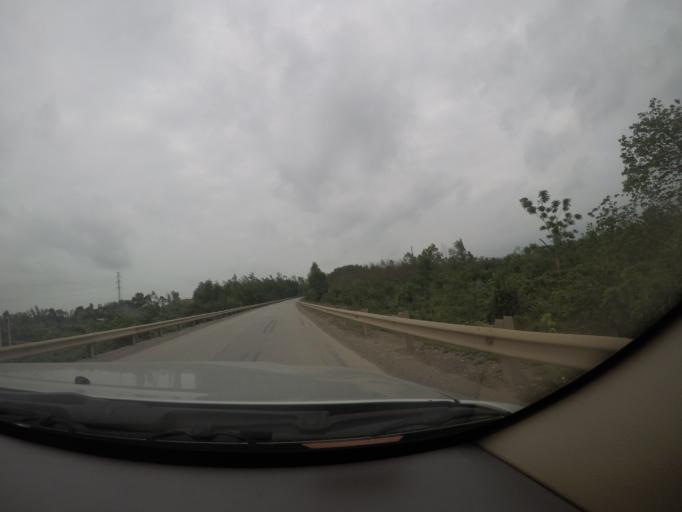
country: VN
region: Quang Binh
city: Quan Hau
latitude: 17.3116
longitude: 106.6355
